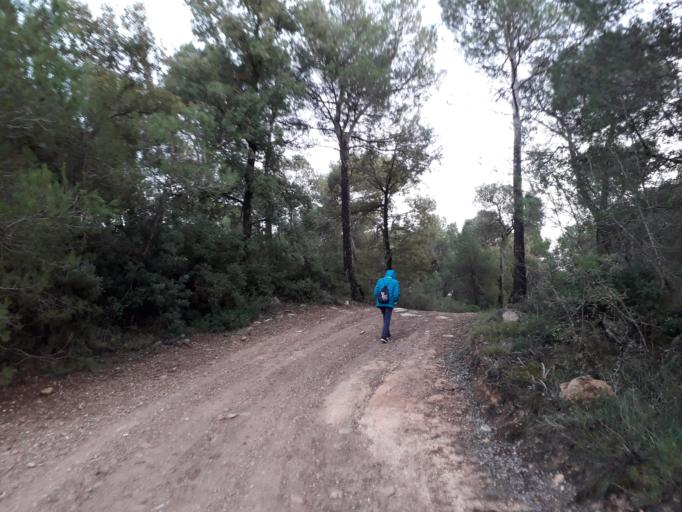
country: ES
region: Catalonia
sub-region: Provincia de Barcelona
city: Jorba
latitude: 41.6100
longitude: 1.5612
